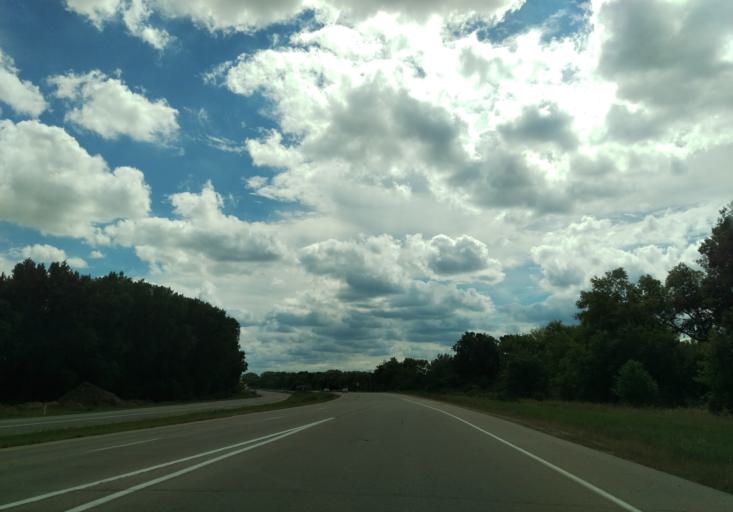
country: US
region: Wisconsin
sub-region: Dane County
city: Maple Bluff
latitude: 43.1533
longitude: -89.4041
